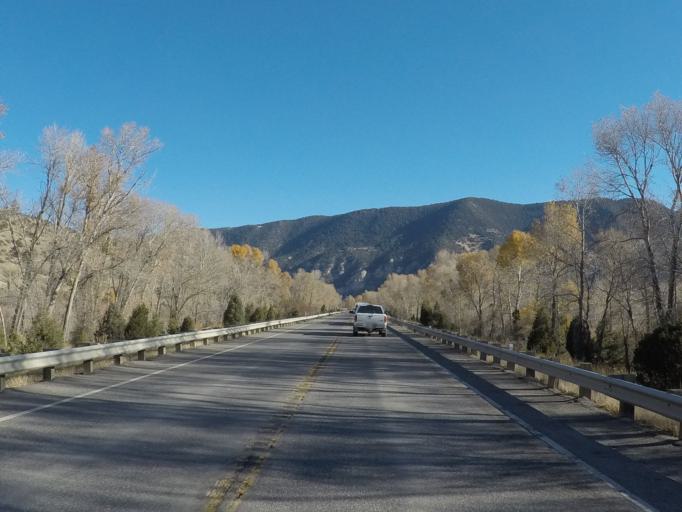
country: US
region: Montana
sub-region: Park County
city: Livingston
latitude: 45.5799
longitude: -110.5807
